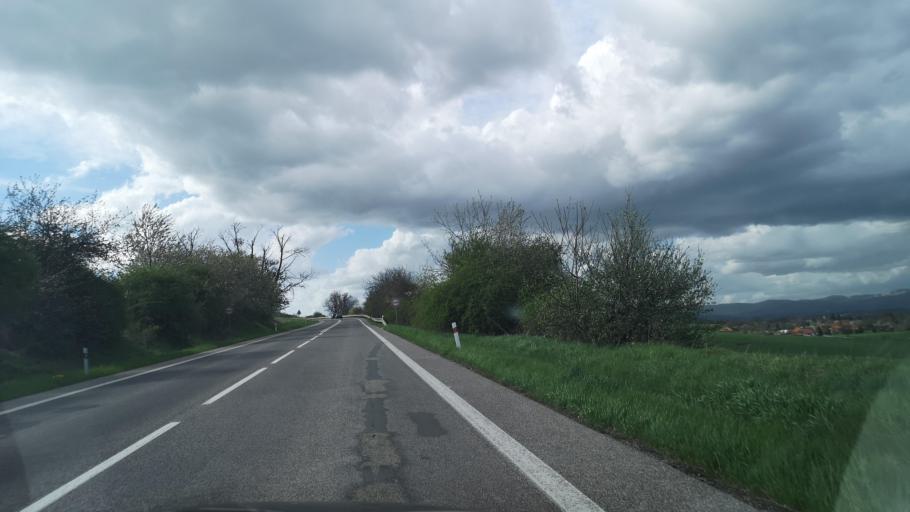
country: SK
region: Nitriansky
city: Zlate Moravce
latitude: 48.3430
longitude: 18.3246
